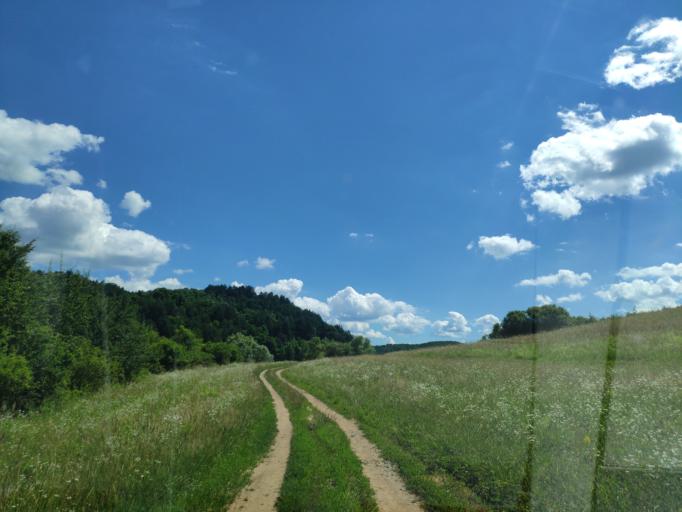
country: HU
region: Borsod-Abauj-Zemplen
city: Arlo
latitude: 48.2666
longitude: 20.1969
